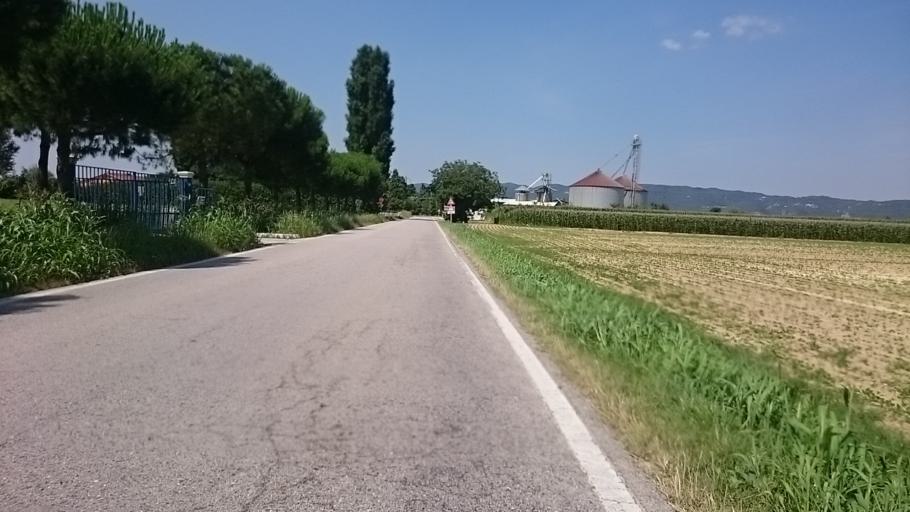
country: IT
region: Veneto
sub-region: Provincia di Vicenza
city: Montegaldella
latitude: 45.4444
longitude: 11.6484
